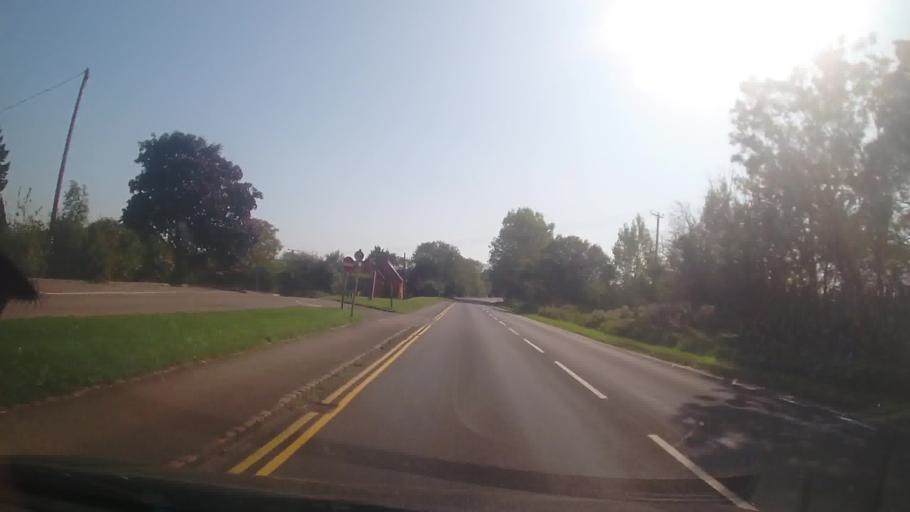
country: GB
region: England
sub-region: Worcestershire
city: Badsey
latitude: 52.0669
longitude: -1.8978
